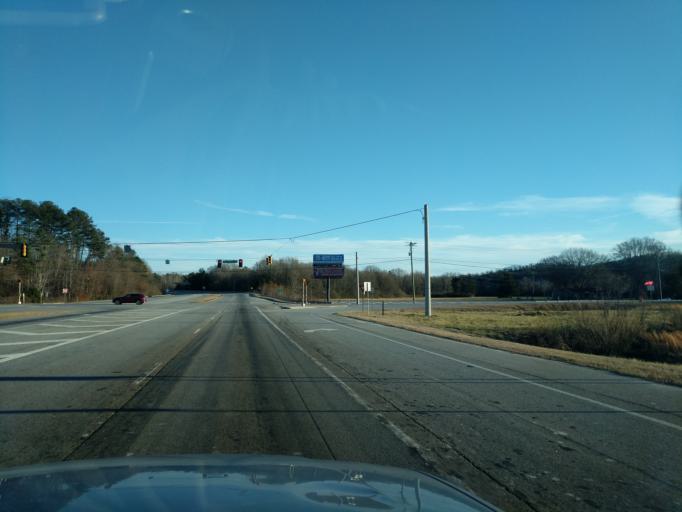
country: US
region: Georgia
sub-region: Stephens County
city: Toccoa
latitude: 34.5429
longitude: -83.3626
